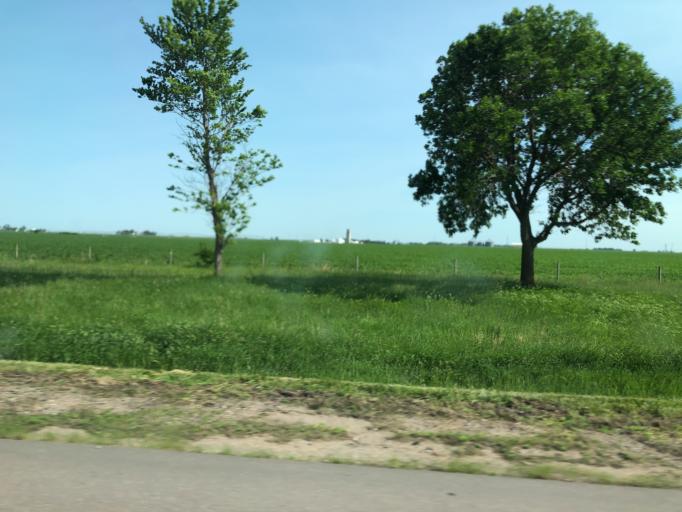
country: US
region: Nebraska
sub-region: York County
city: York
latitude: 40.8210
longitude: -97.5937
